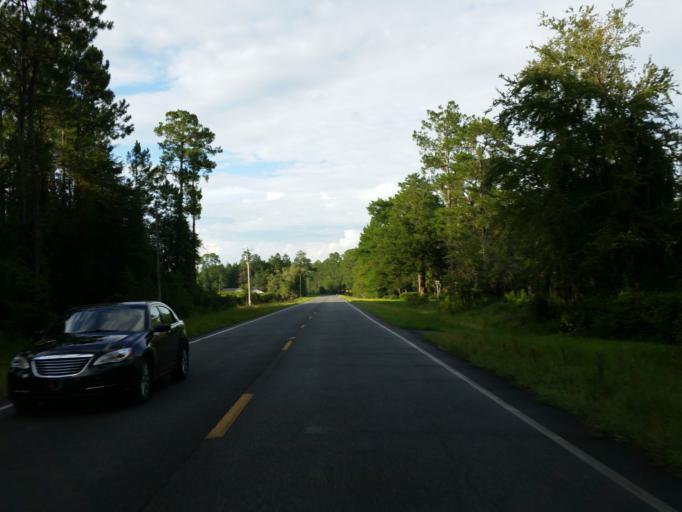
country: US
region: Georgia
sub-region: Clinch County
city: Homerville
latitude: 30.6684
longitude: -82.5557
